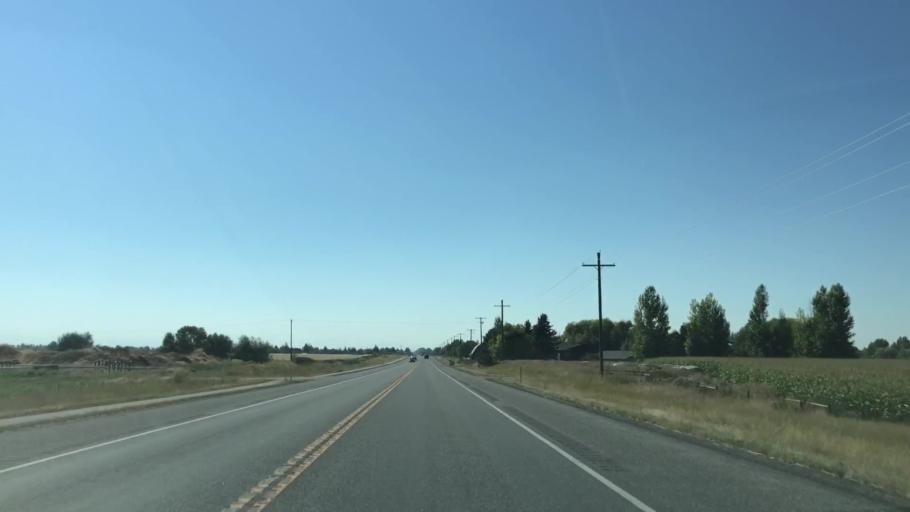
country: US
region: Montana
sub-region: Gallatin County
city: Belgrade
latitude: 45.7292
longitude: -111.1117
